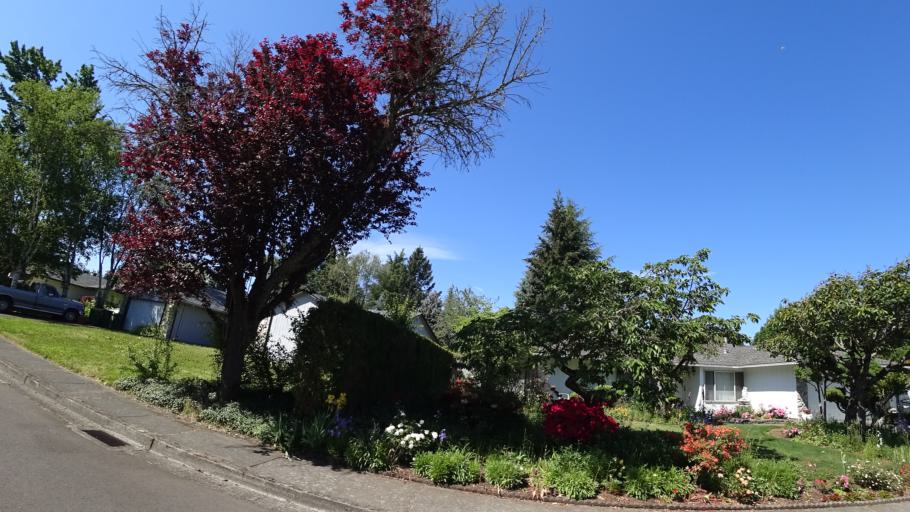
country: US
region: Oregon
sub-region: Washington County
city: Beaverton
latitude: 45.4544
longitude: -122.7988
